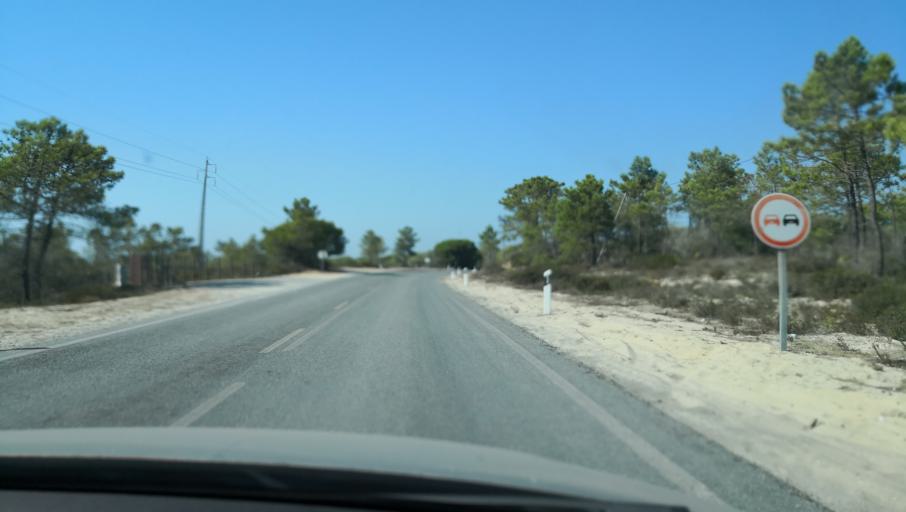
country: PT
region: Setubal
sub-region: Setubal
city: Setubal
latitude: 38.3859
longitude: -8.7993
